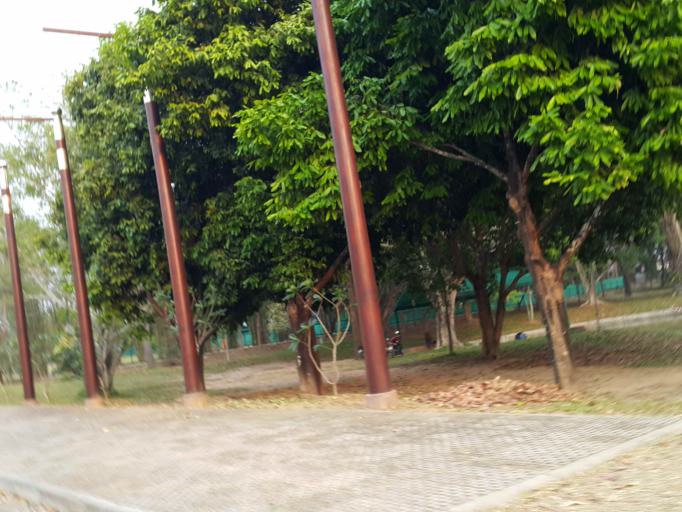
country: TH
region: Chiang Mai
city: San Sai
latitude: 18.9110
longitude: 99.0123
